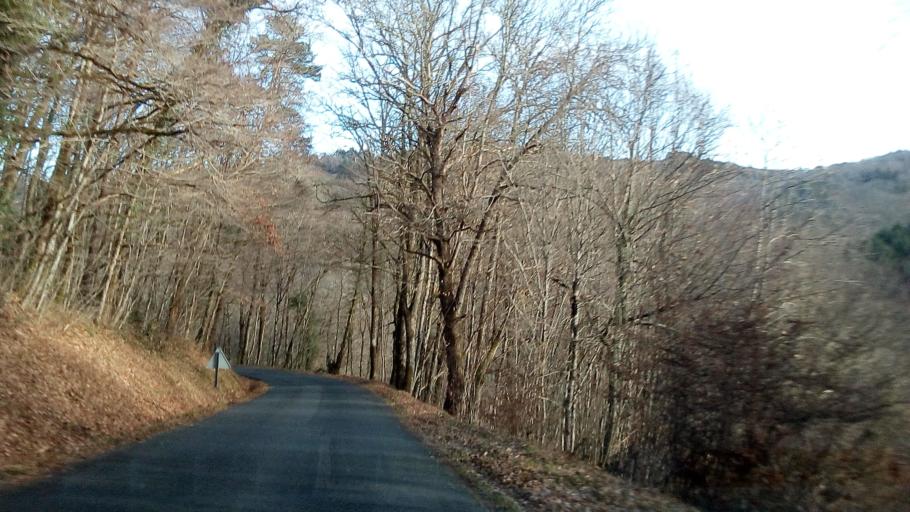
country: FR
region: Limousin
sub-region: Departement de la Correze
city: Naves
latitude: 45.2989
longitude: 1.7971
